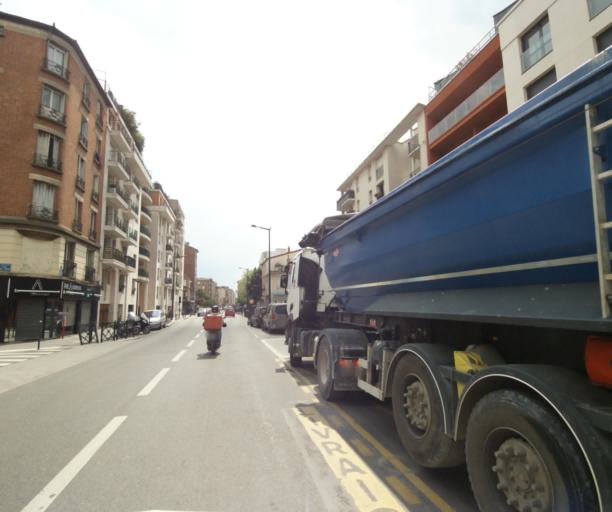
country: FR
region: Ile-de-France
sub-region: Departement des Hauts-de-Seine
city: Bois-Colombes
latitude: 48.9228
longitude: 2.2764
